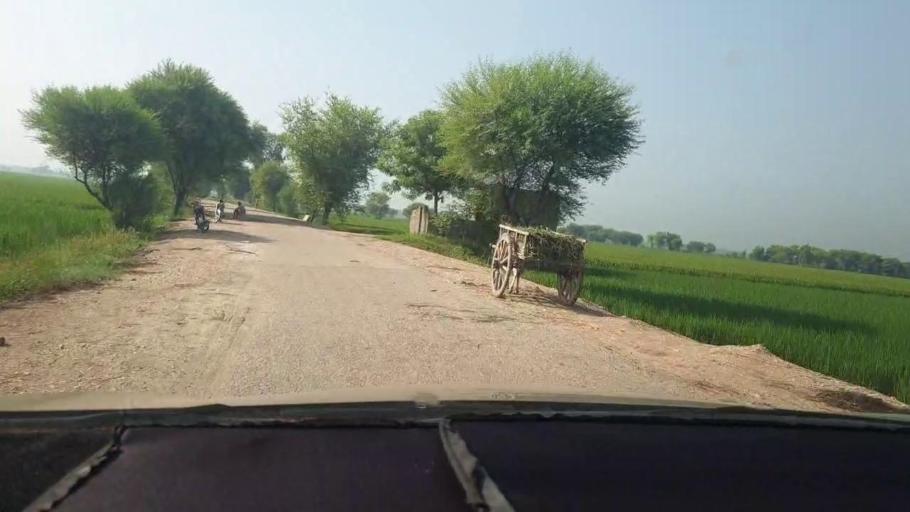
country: PK
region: Sindh
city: Kambar
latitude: 27.6258
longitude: 68.0892
